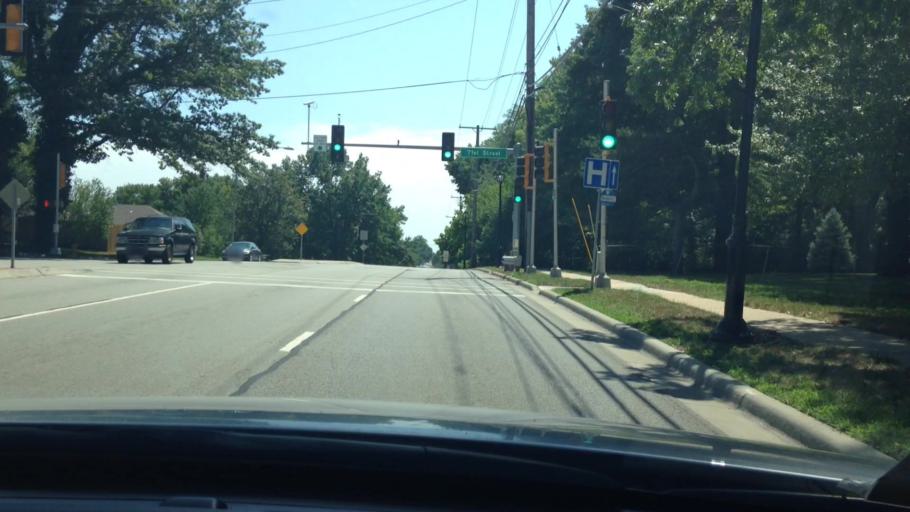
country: US
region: Kansas
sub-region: Johnson County
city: Merriam
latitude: 39.0007
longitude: -94.6865
